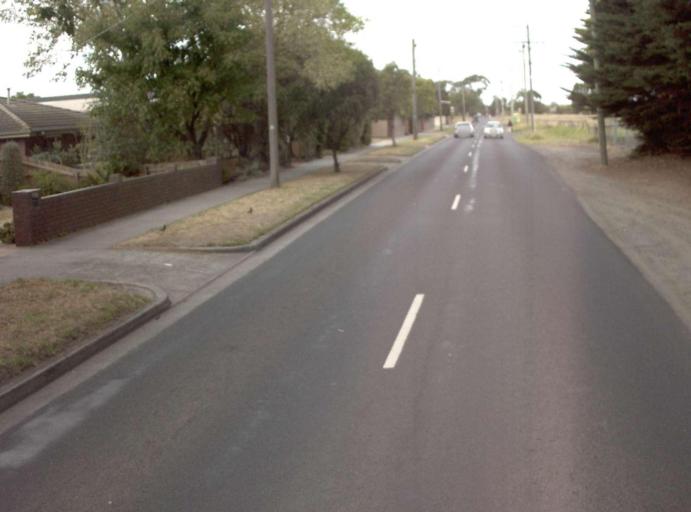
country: AU
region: Victoria
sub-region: Monash
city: Oakleigh South
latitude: -37.9415
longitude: 145.0977
